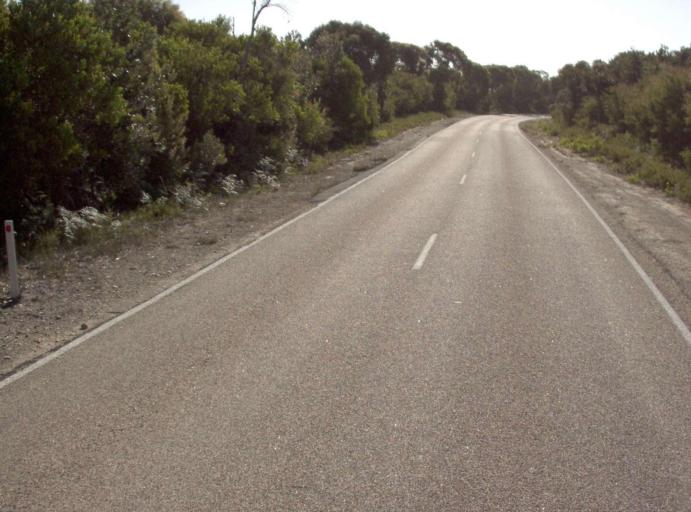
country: AU
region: Victoria
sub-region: East Gippsland
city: Lakes Entrance
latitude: -37.8007
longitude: 148.6105
